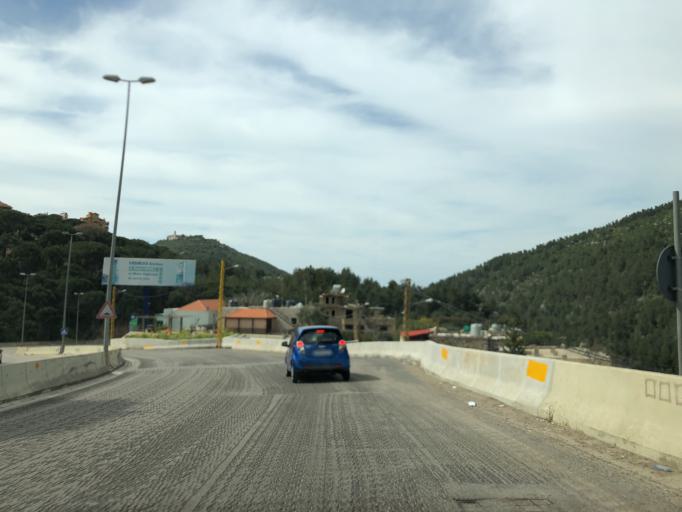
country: LB
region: Mont-Liban
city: Bhamdoun el Mhatta
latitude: 33.8920
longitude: 35.6594
